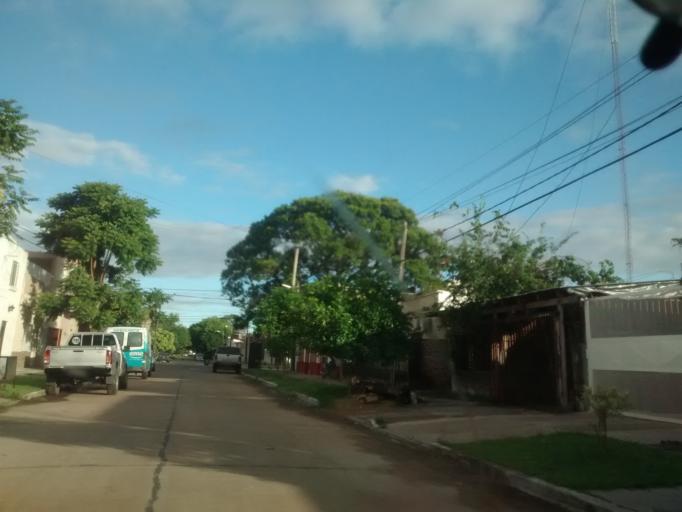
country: AR
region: Chaco
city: Resistencia
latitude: -27.4570
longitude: -59.0007
